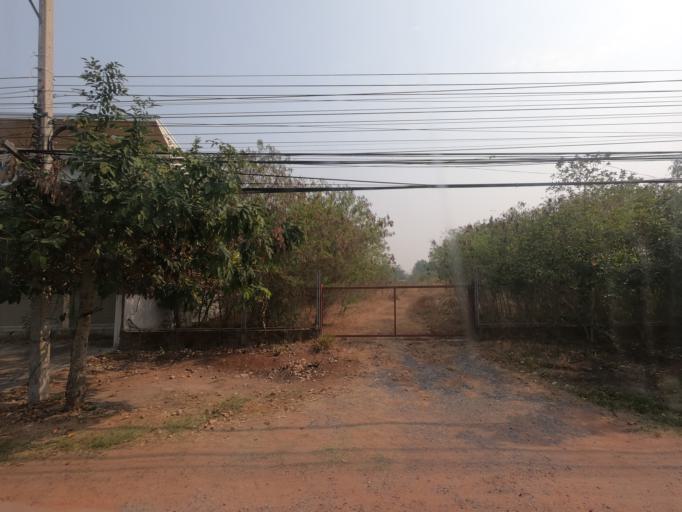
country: TH
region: Khon Kaen
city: Ban Phai
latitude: 16.0669
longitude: 102.7219
